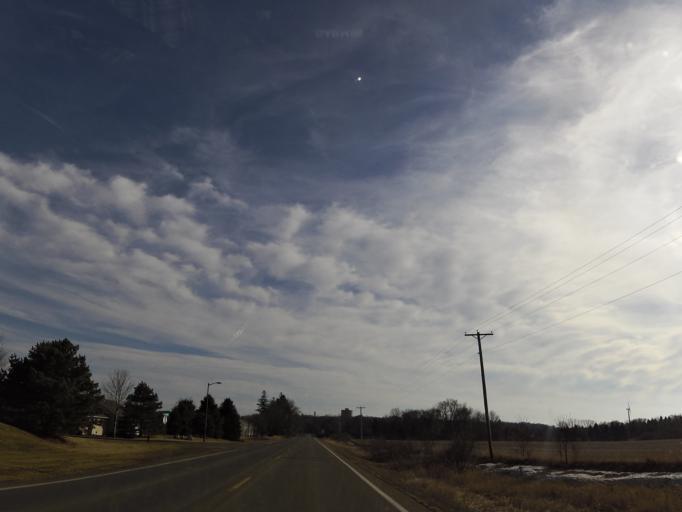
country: US
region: Minnesota
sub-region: Rice County
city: Northfield
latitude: 44.4746
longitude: -93.1808
